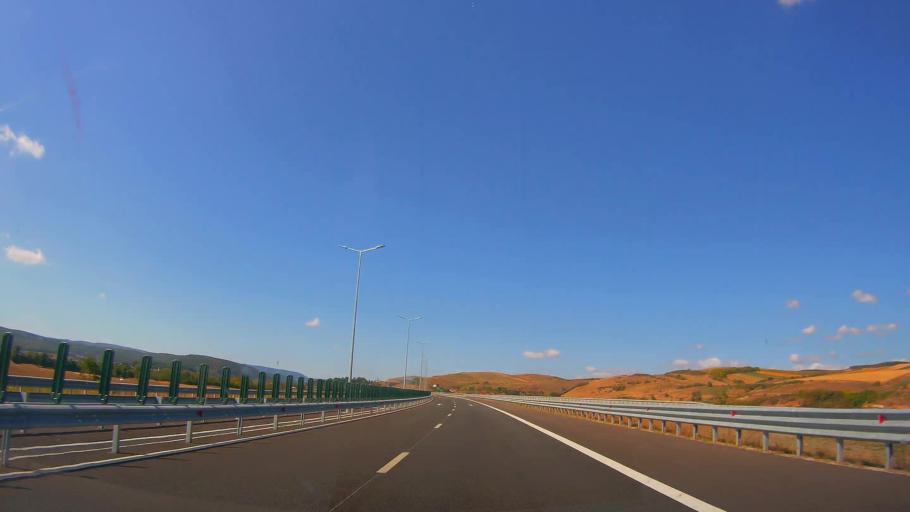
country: RO
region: Cluj
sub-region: Comuna Floresti
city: Luna de Sus
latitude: 46.7565
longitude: 23.4090
